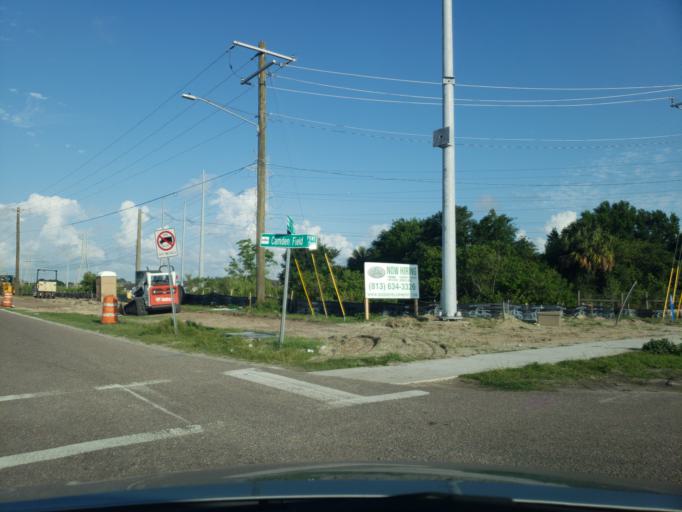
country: US
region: Florida
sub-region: Hillsborough County
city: Progress Village
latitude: 27.9084
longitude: -82.3686
